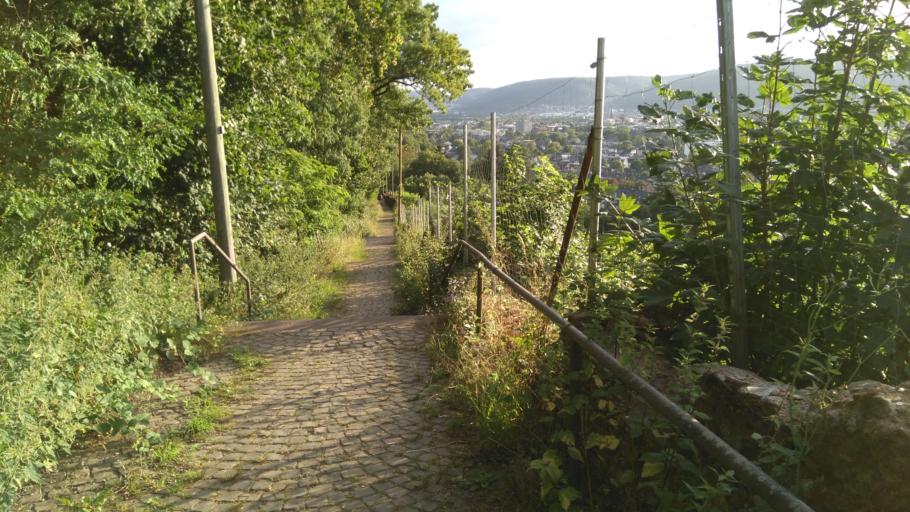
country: DE
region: Rheinland-Pfalz
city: Trier
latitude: 49.7542
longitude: 6.6587
